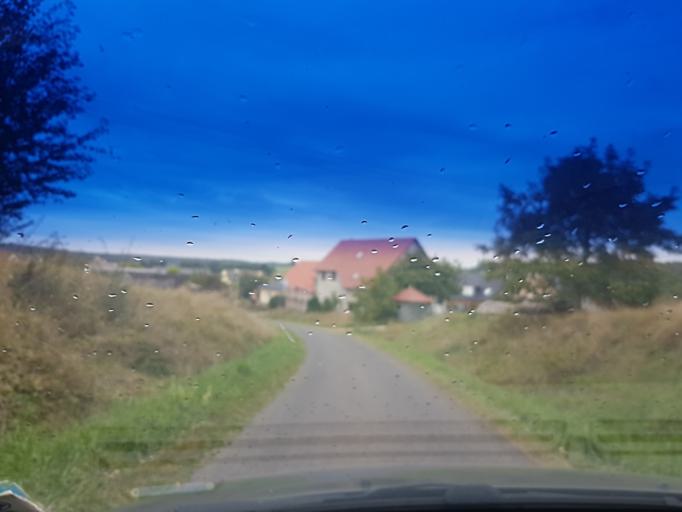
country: DE
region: Bavaria
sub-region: Regierungsbezirk Unterfranken
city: Geiselwind
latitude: 49.8301
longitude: 10.4816
